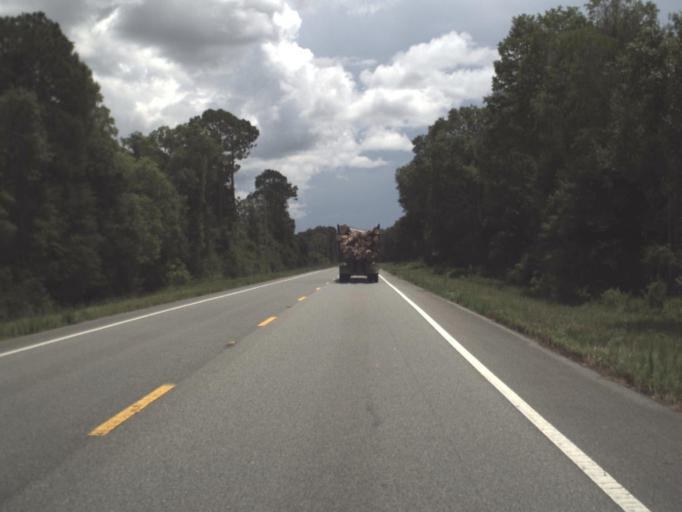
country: US
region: Florida
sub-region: Taylor County
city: Perry
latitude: 30.0958
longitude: -83.6877
